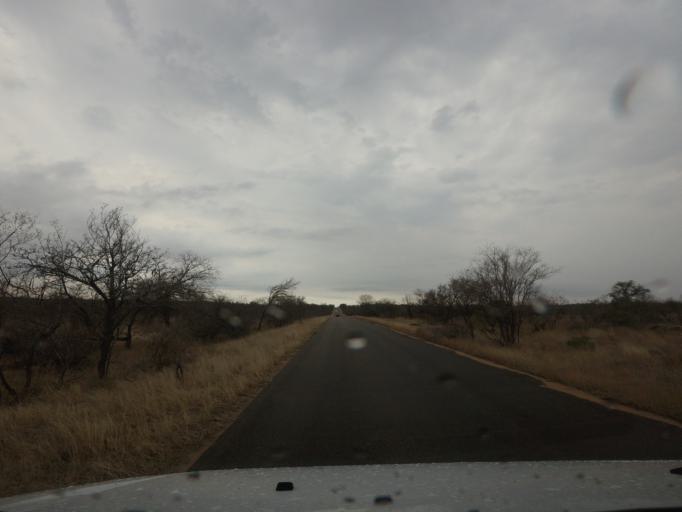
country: ZA
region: Limpopo
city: Thulamahashi
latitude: -24.4730
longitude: 31.4139
